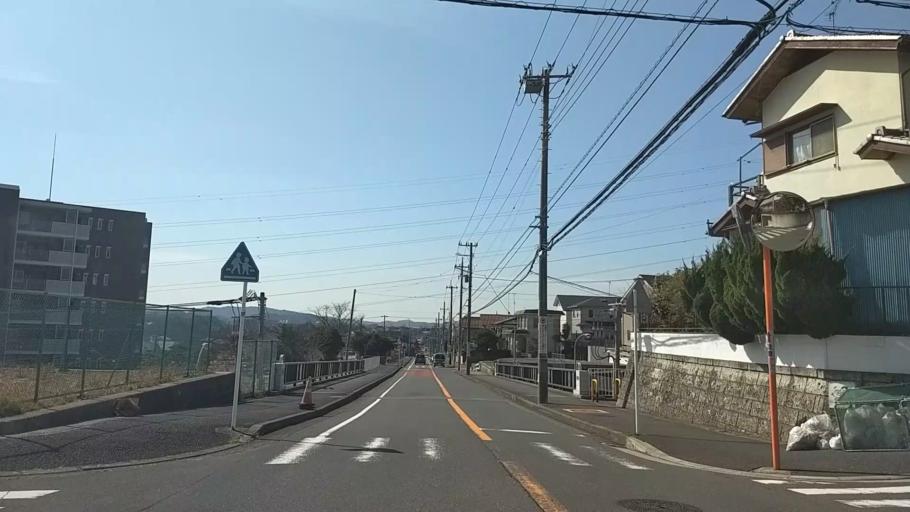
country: JP
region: Kanagawa
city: Kamakura
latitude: 35.3796
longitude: 139.5505
